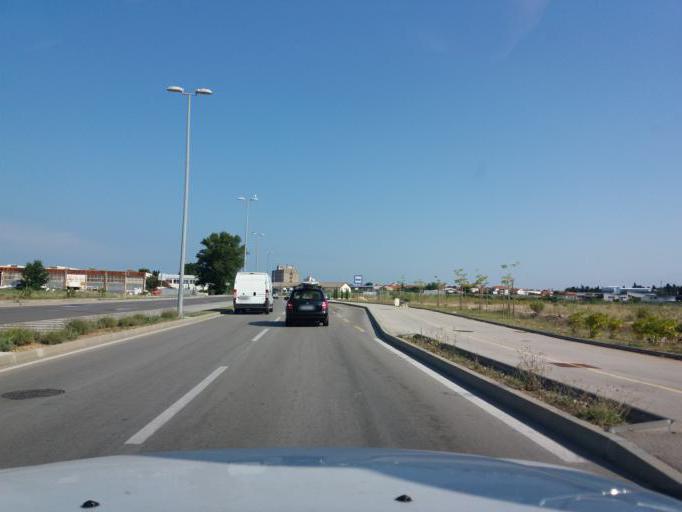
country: HR
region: Zadarska
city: Zadar
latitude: 44.0968
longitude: 15.2578
